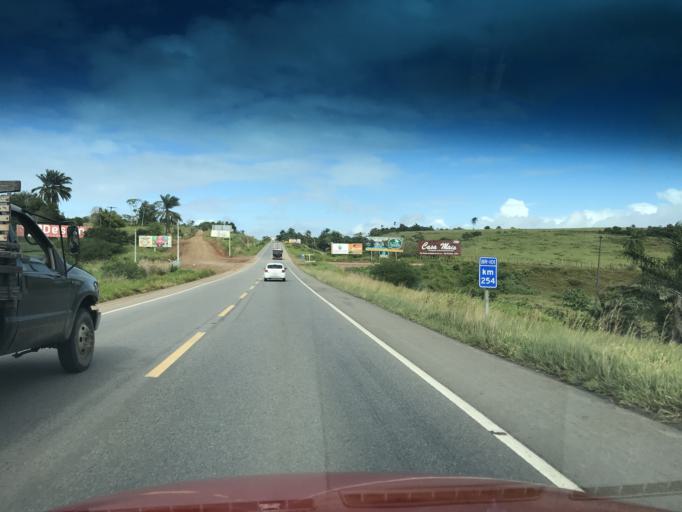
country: BR
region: Bahia
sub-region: Conceicao Do Almeida
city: Muritiba
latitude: -12.9147
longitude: -39.2434
